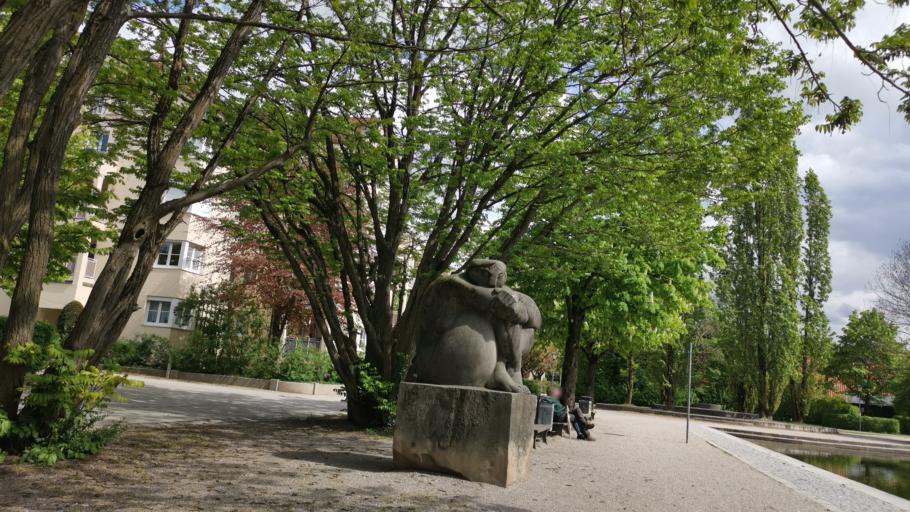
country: DE
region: Bavaria
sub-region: Upper Bavaria
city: Bogenhausen
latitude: 48.1724
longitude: 11.5911
